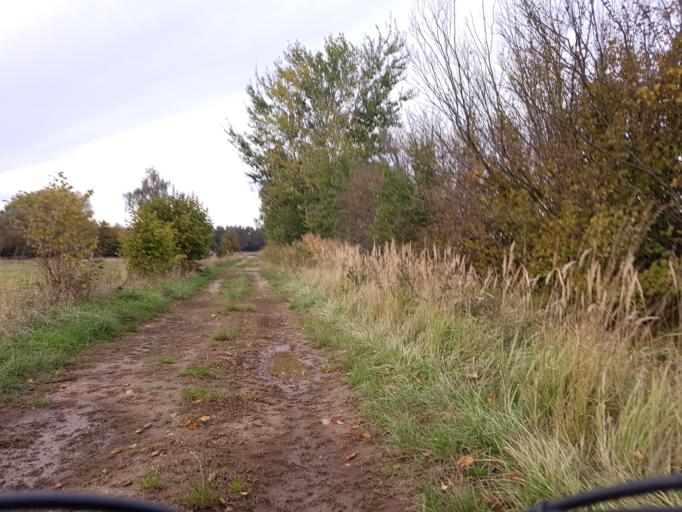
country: DE
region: Brandenburg
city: Schilda
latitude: 51.6048
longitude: 13.3806
